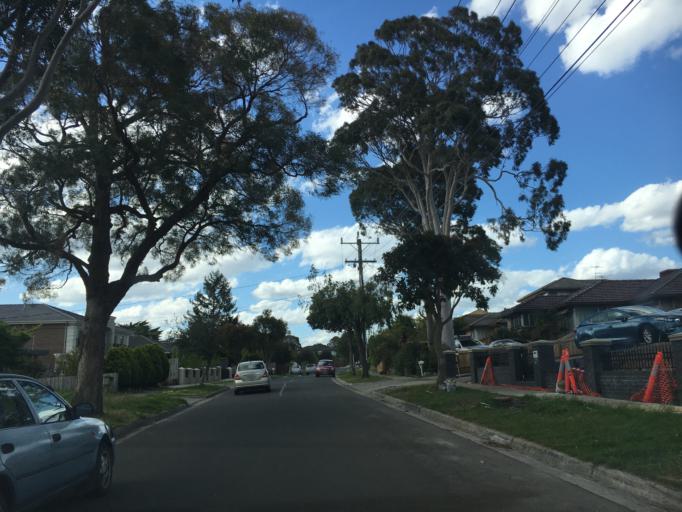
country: AU
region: Victoria
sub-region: Monash
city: Notting Hill
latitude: -37.8929
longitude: 145.1686
